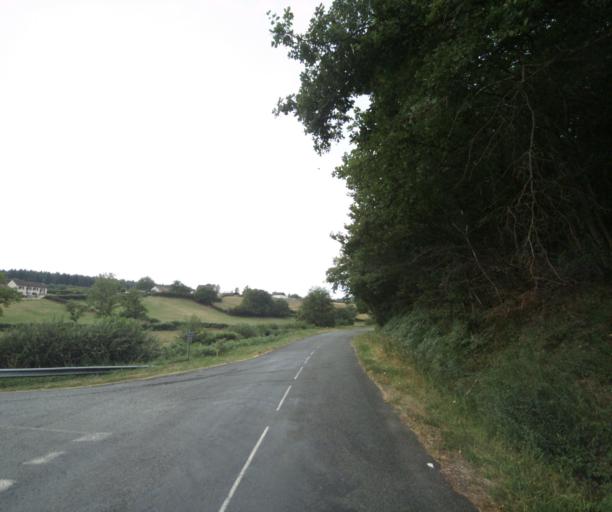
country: FR
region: Bourgogne
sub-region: Departement de Saone-et-Loire
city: Gueugnon
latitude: 46.5867
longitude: 4.0135
